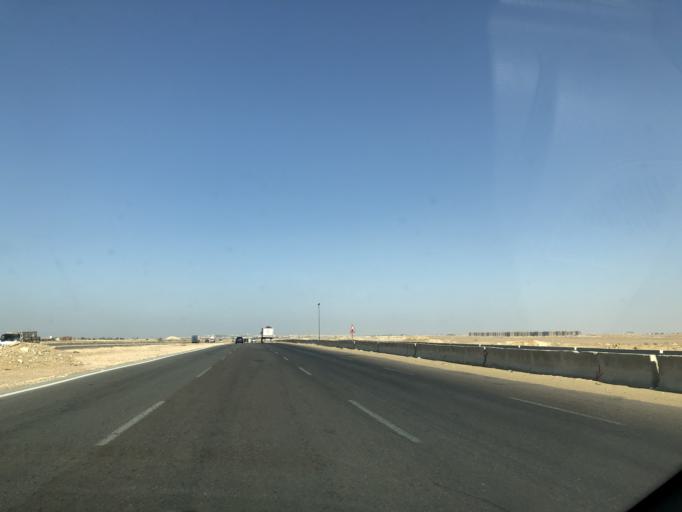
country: EG
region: Muhafazat al Minufiyah
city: Ashmun
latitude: 30.0677
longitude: 30.8683
